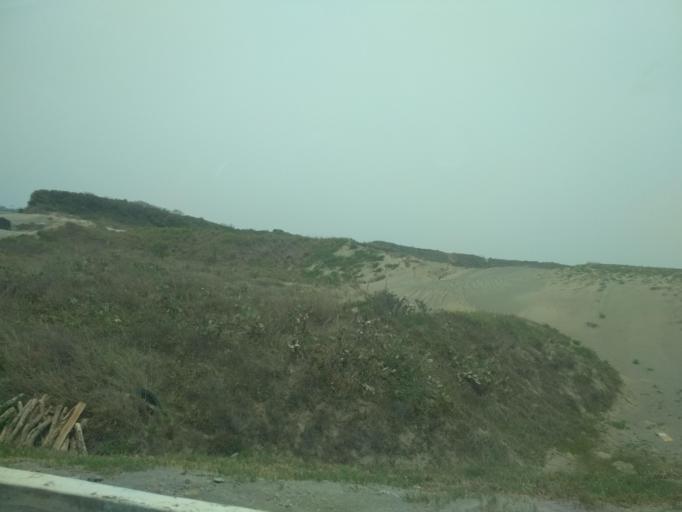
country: MX
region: Veracruz
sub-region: Alvarado
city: Playa de la Libertad
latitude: 19.0566
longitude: -96.0556
